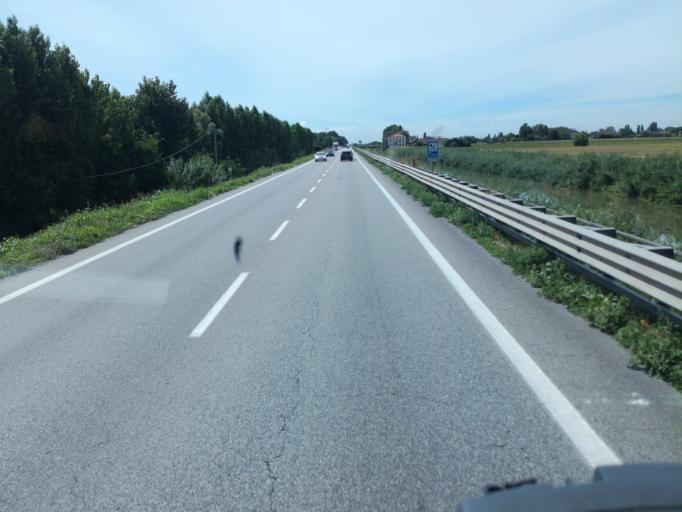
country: IT
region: Veneto
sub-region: Provincia di Venezia
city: Campagna Lupia
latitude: 45.3318
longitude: 12.1344
